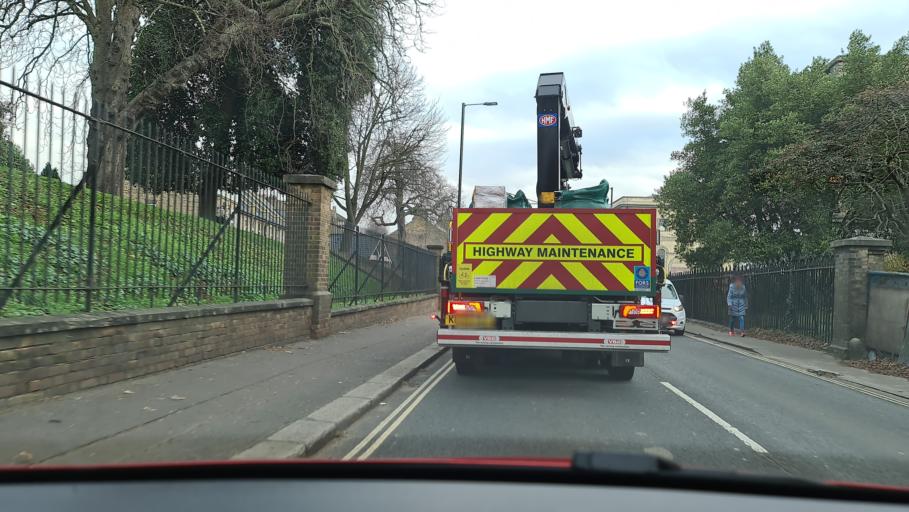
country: GB
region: England
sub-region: Greater London
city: Hampton
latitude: 51.4133
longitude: -0.3695
